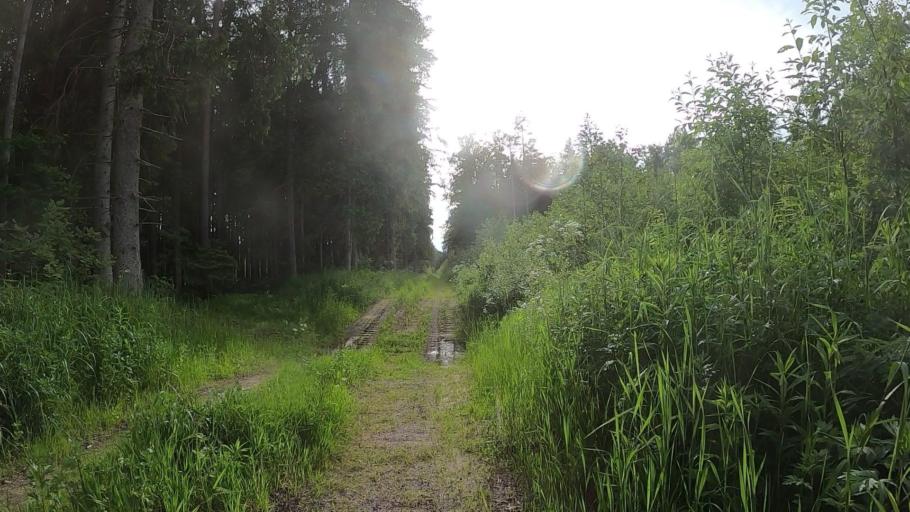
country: LV
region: Ozolnieku
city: Ozolnieki
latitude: 56.7371
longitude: 23.7901
